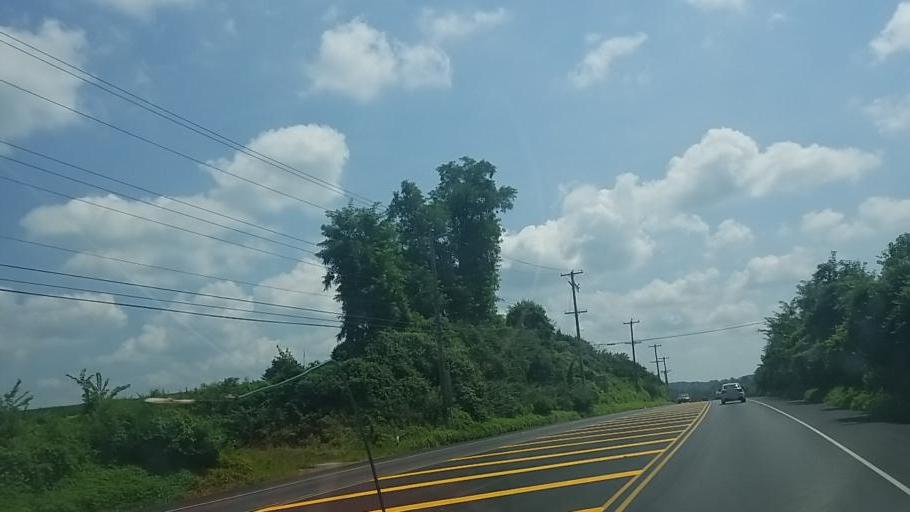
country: US
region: Pennsylvania
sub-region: Chester County
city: Avondale
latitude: 39.8396
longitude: -75.8022
